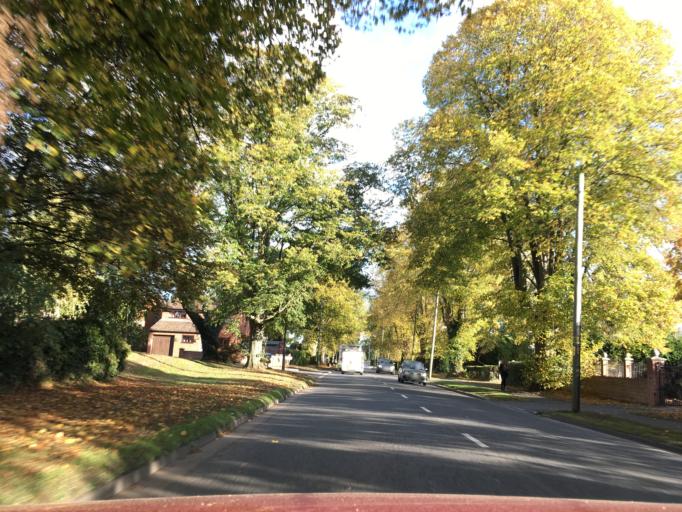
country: GB
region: England
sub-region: Herefordshire
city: Belmont
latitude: 52.0654
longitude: -2.7529
